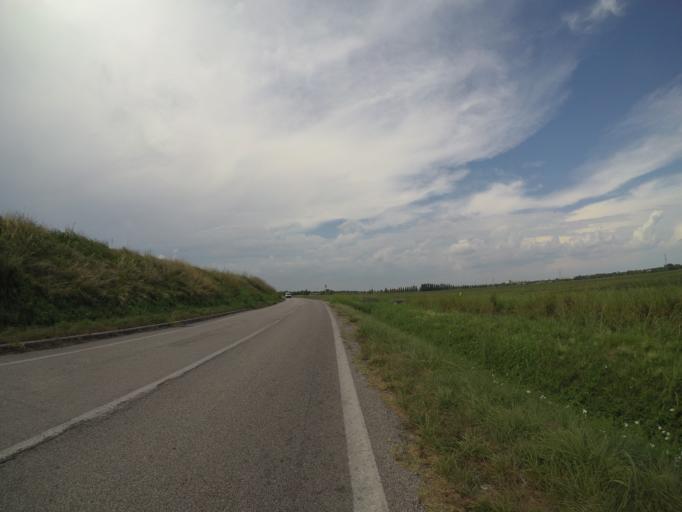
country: IT
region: Friuli Venezia Giulia
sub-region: Provincia di Udine
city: Pertegada
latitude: 45.6792
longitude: 13.0651
